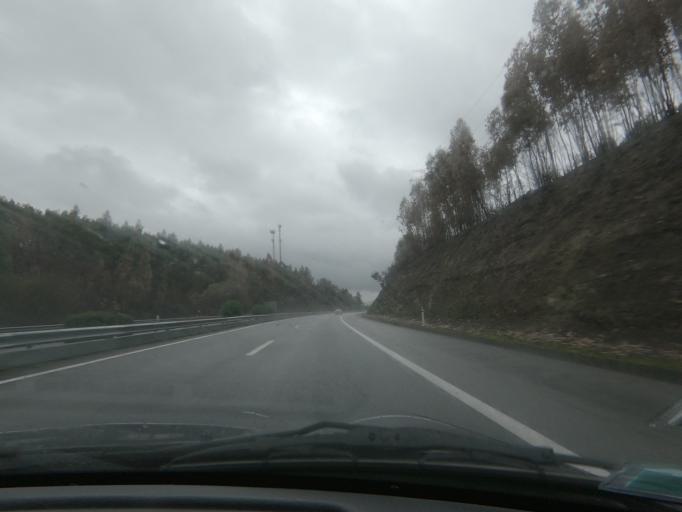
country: PT
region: Porto
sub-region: Paredes
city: Baltar
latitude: 41.1743
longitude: -8.3789
